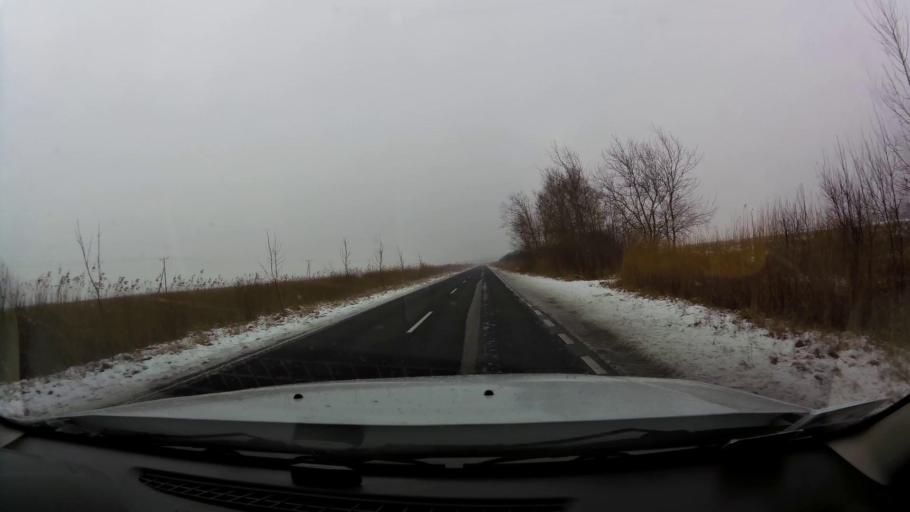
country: PL
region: West Pomeranian Voivodeship
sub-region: Powiat gryficki
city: Mrzezyno
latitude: 54.1270
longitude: 15.2743
